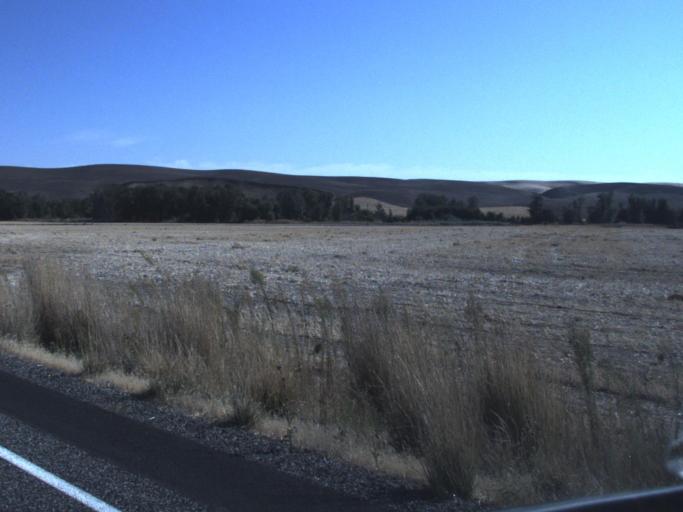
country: US
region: Washington
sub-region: Walla Walla County
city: Walla Walla
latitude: 46.2991
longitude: -118.3925
